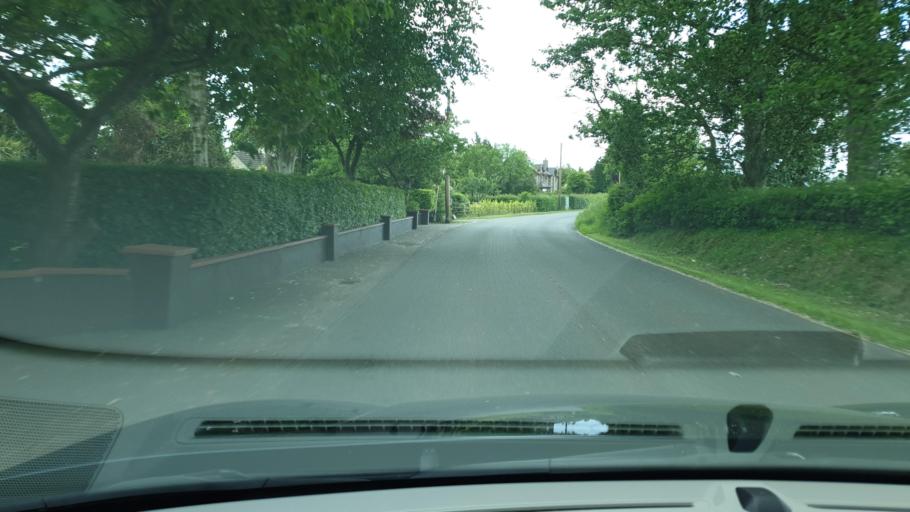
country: IE
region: Leinster
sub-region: An Mhi
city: Dunboyne
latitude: 53.4022
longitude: -6.4691
